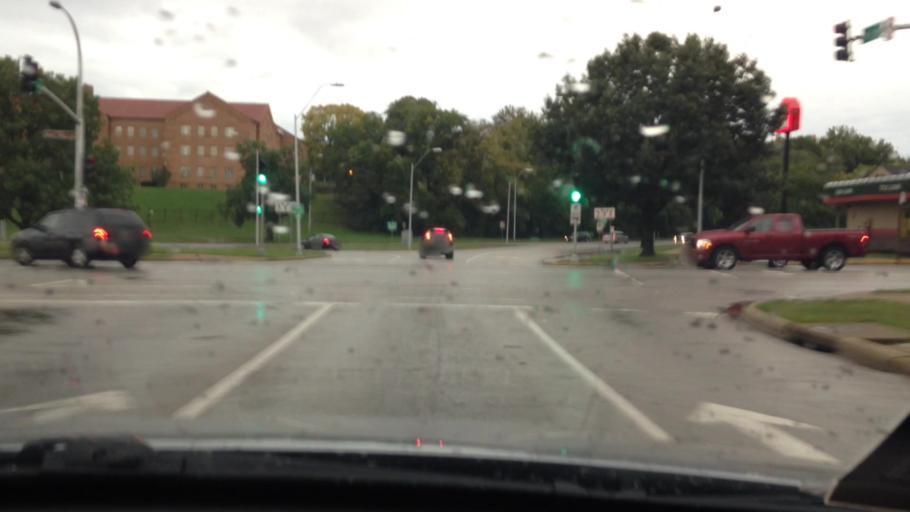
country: US
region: Kansas
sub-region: Johnson County
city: Mission Hills
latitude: 39.0134
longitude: -94.5704
